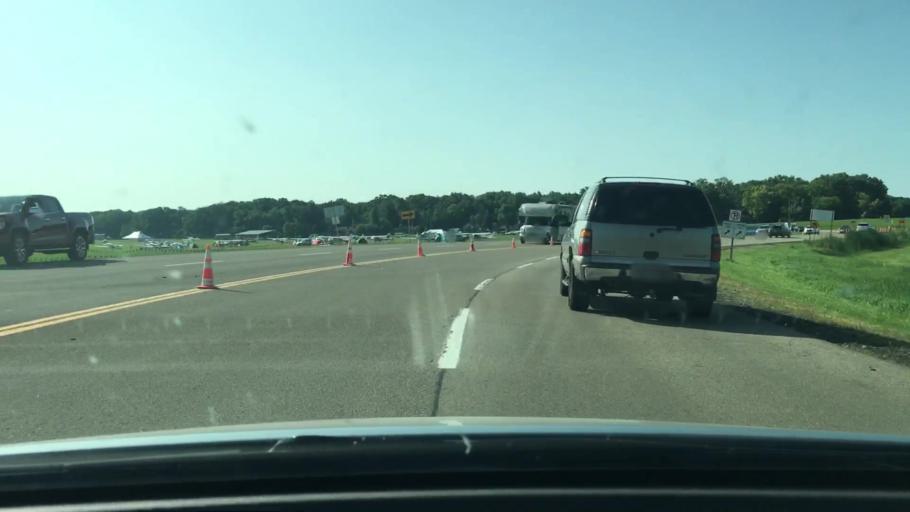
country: US
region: Wisconsin
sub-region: Winnebago County
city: Oshkosh
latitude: 43.9920
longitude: -88.5782
